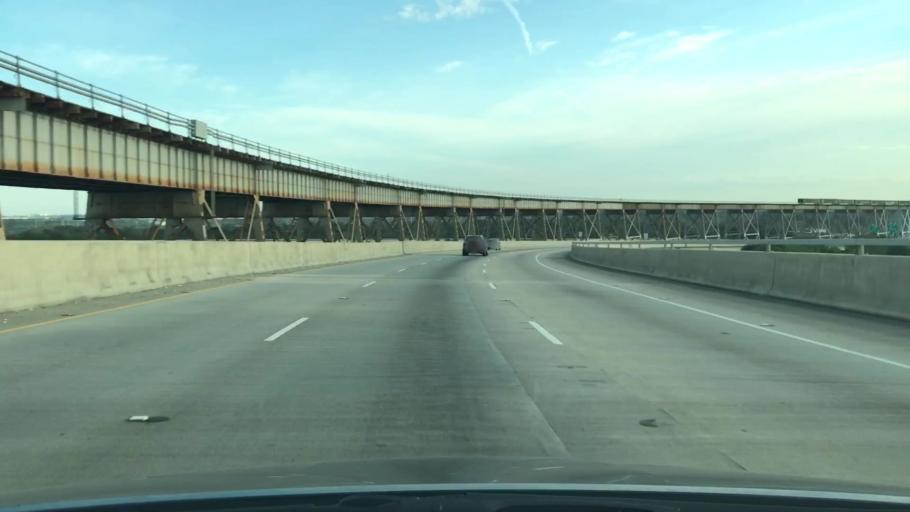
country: US
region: Louisiana
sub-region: Jefferson Parish
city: Bridge City
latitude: 29.9391
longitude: -90.1638
